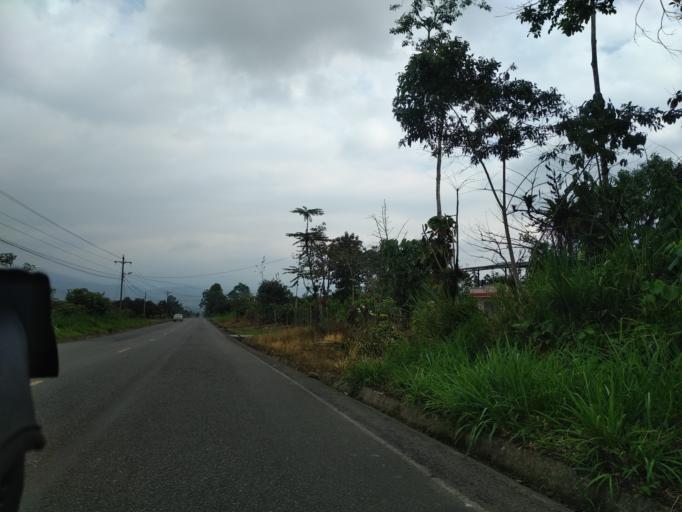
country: EC
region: Cotopaxi
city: La Mana
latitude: -0.8843
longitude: -79.1610
